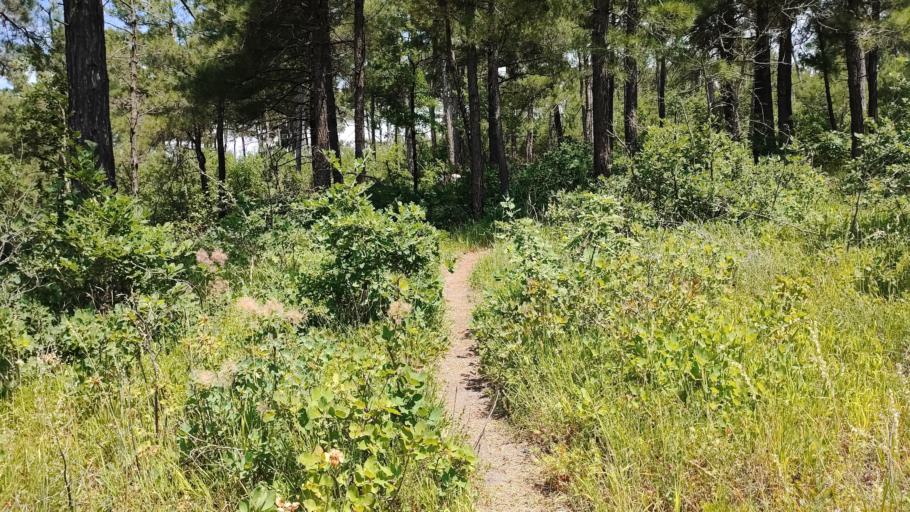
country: RU
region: Krasnodarskiy
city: Divnomorskoye
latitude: 44.4789
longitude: 38.1416
